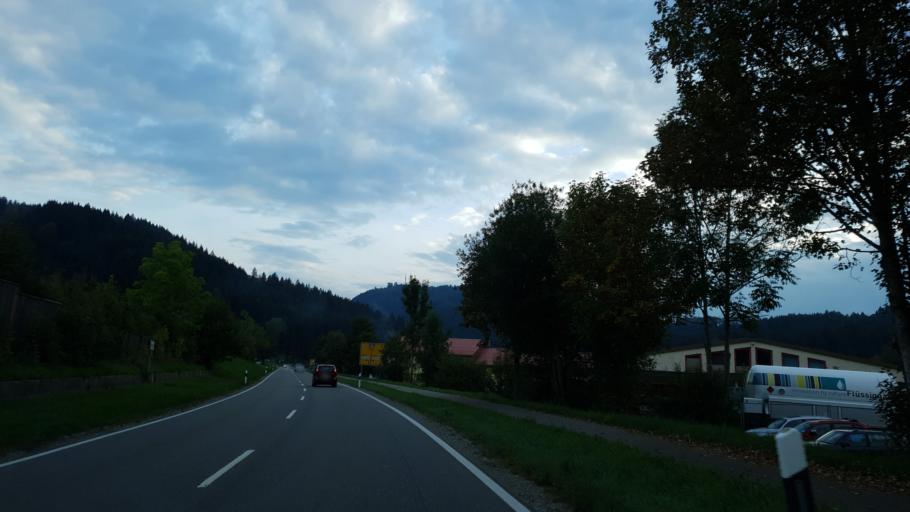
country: DE
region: Bavaria
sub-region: Swabia
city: Weitnau
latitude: 47.6590
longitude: 10.0903
